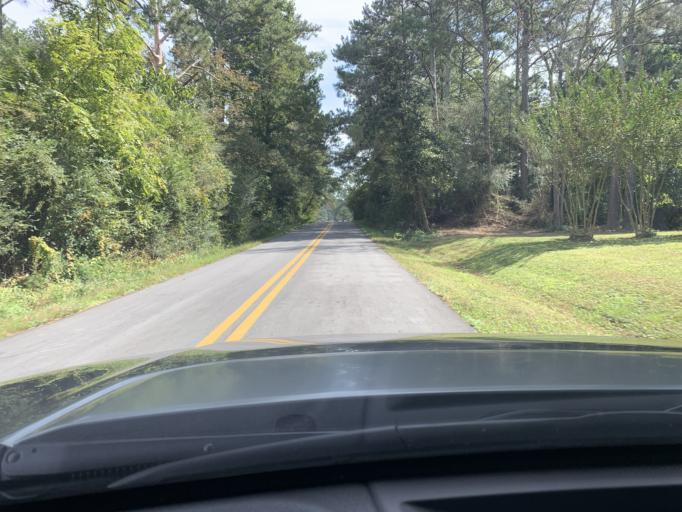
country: US
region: Georgia
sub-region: Polk County
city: Cedartown
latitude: 33.9482
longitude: -85.3786
